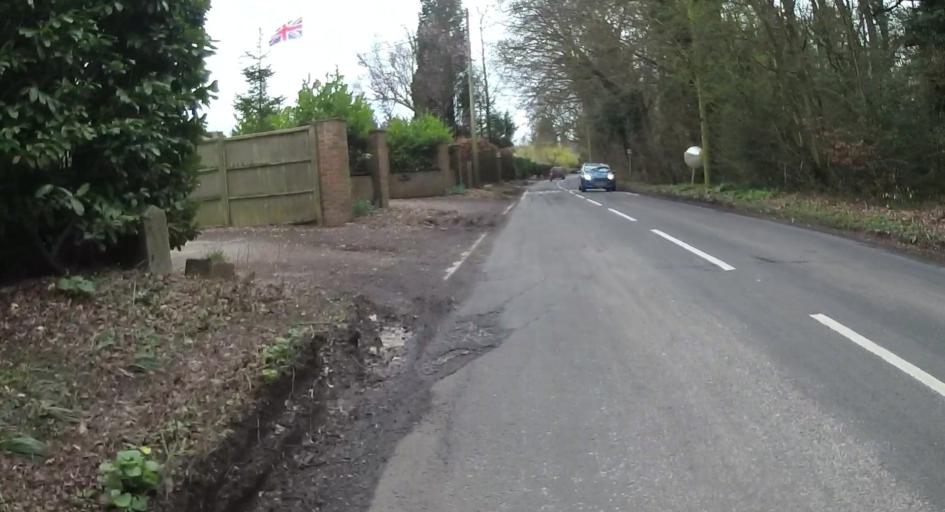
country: GB
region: England
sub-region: Hampshire
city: Alton
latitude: 51.1742
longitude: -0.9808
